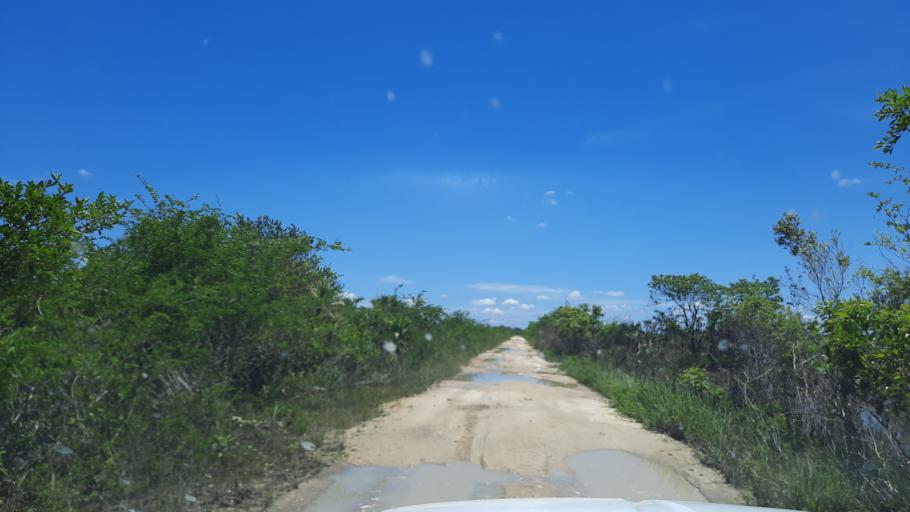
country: BZ
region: Cayo
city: Belmopan
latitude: 17.3814
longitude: -88.4921
